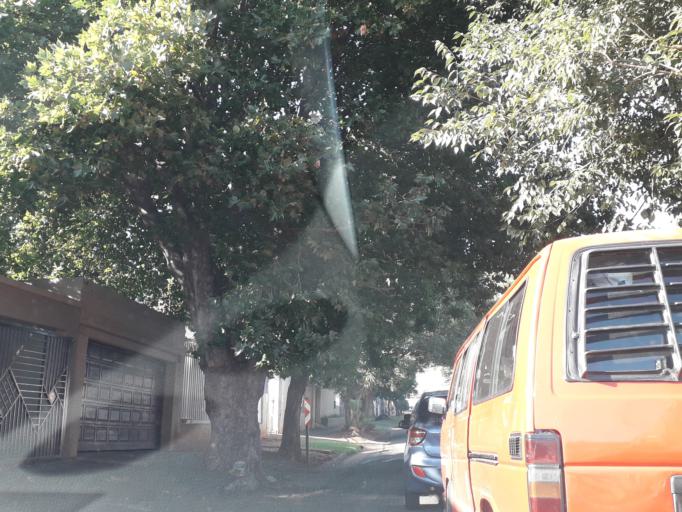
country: ZA
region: Gauteng
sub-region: City of Johannesburg Metropolitan Municipality
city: Johannesburg
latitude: -26.1831
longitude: 27.9827
